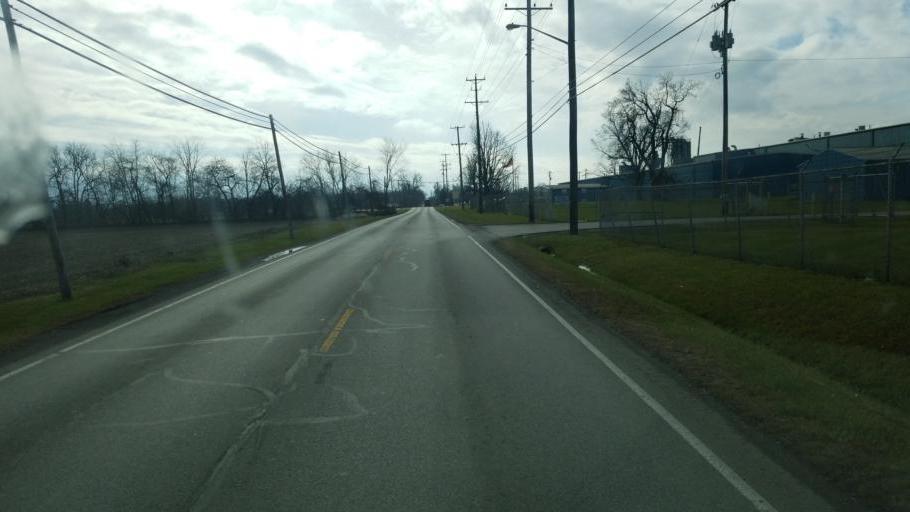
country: US
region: Ohio
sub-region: Delaware County
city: Delaware
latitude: 40.2864
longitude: -83.0800
